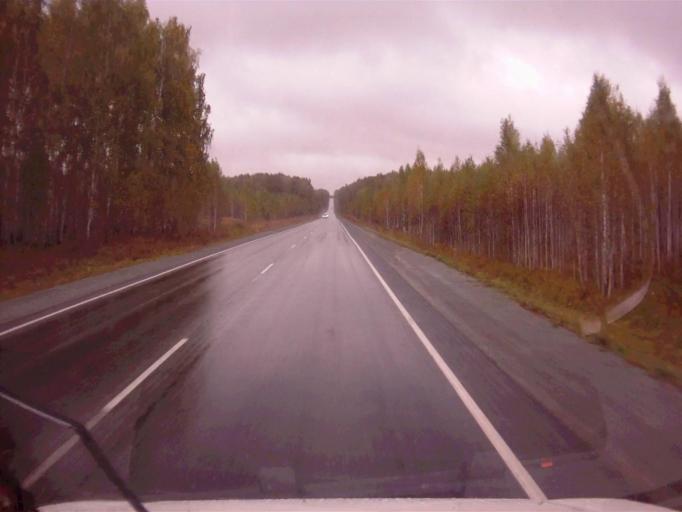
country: RU
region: Chelyabinsk
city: Tayginka
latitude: 55.5143
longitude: 60.6398
